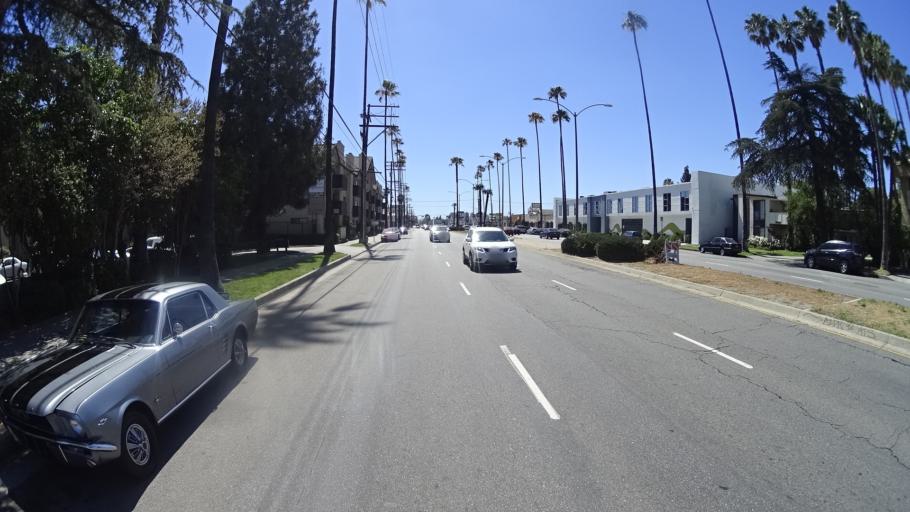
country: US
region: California
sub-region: Los Angeles County
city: Van Nuys
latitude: 34.2011
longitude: -118.4813
